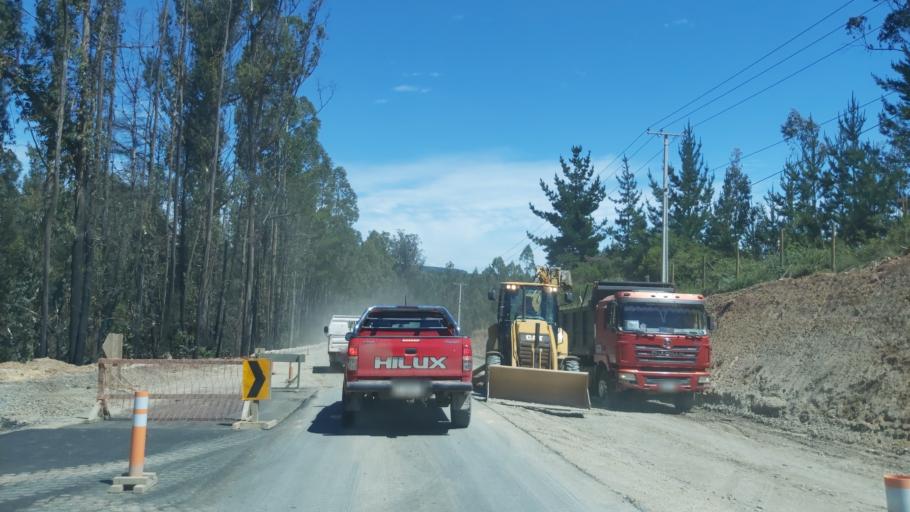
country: CL
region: Maule
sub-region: Provincia de Talca
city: Constitucion
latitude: -35.3853
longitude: -72.4198
